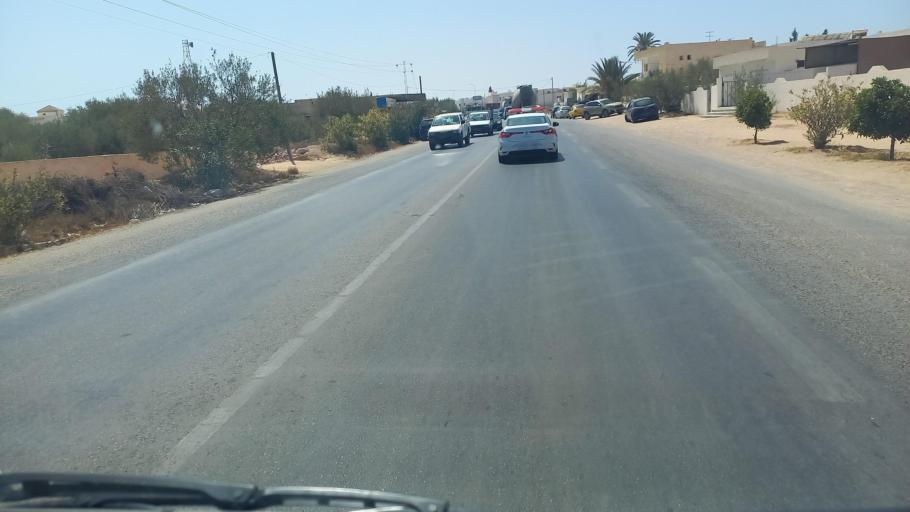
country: TN
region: Madanin
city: Houmt Souk
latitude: 33.8072
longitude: 10.8811
